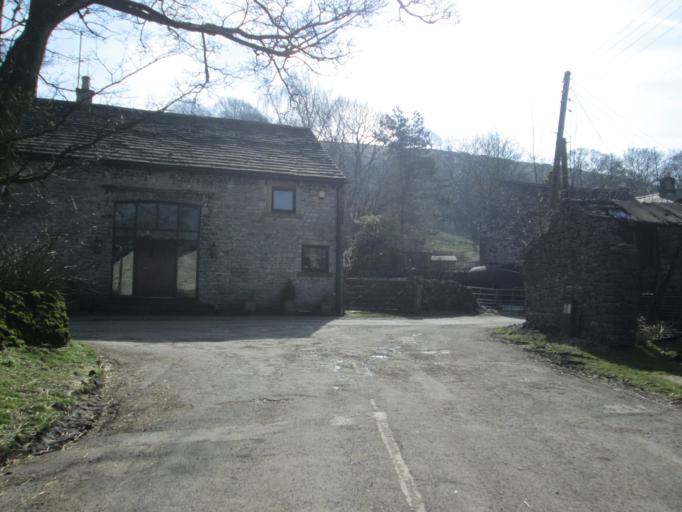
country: GB
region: England
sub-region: Derbyshire
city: Tideswell
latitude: 53.2354
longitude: -1.7802
